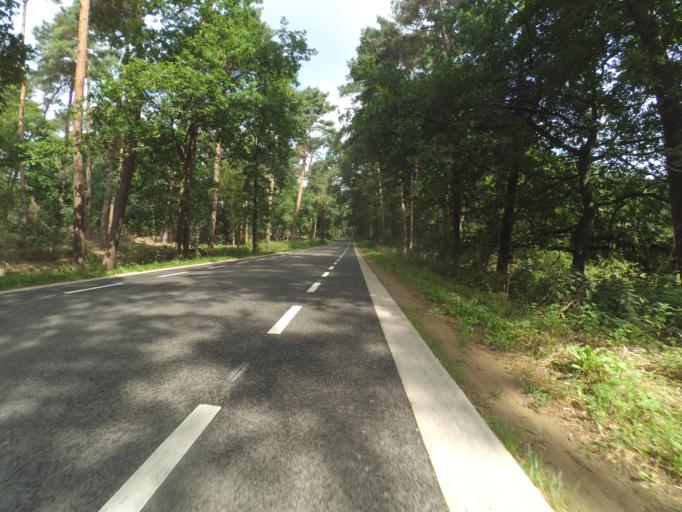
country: NL
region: Limburg
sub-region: Gemeente Roerdalen
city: Montfort
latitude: 51.1308
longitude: 5.9589
